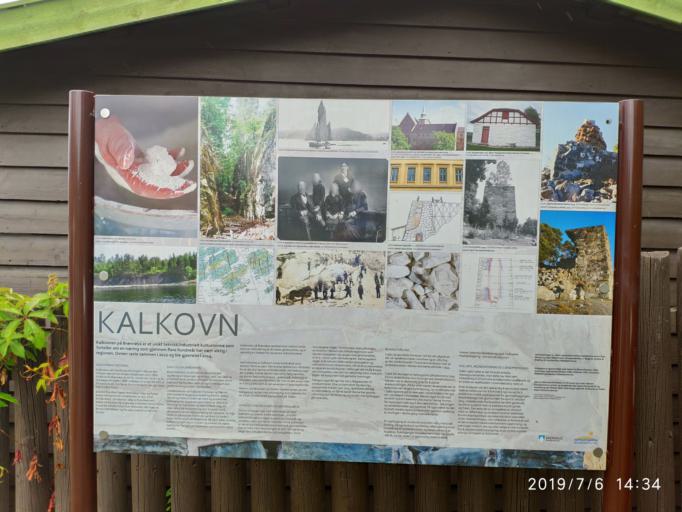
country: NO
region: Akershus
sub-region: Baerum
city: Sandvika
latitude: 59.8572
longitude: 10.5272
